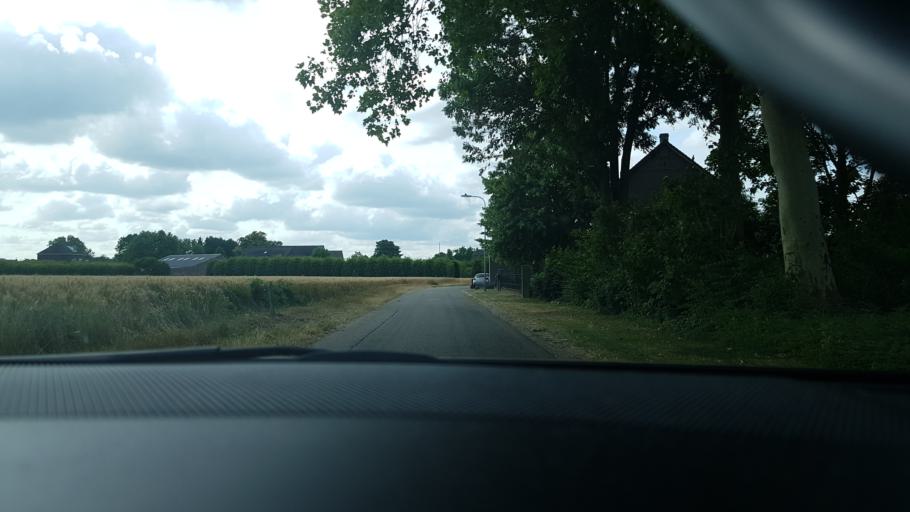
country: NL
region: Limburg
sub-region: Gemeente Beesel
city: Beesel
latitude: 51.2369
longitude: 6.0259
